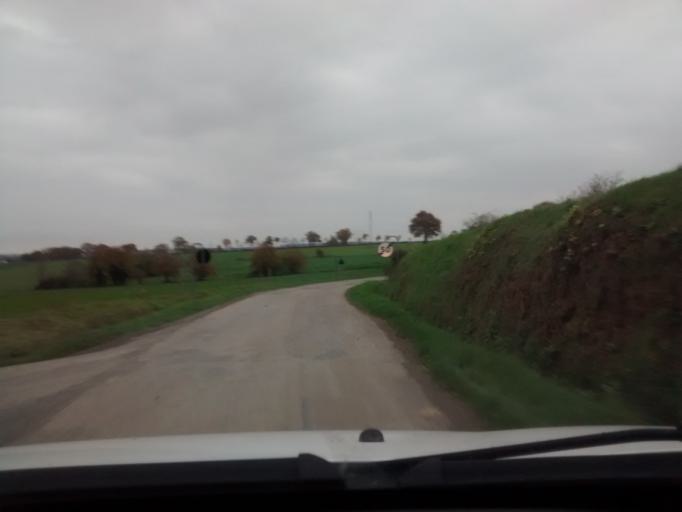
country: FR
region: Brittany
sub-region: Departement d'Ille-et-Vilaine
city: Brece
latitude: 48.1393
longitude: -1.4958
